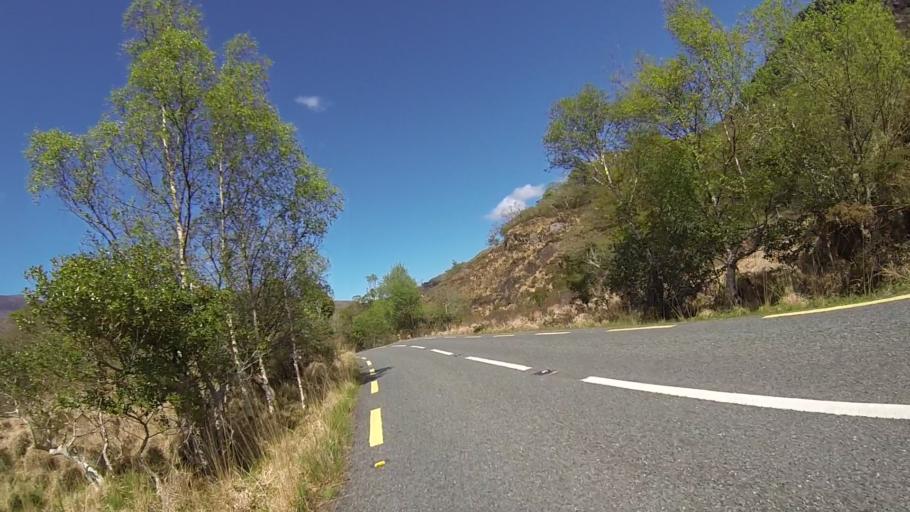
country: IE
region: Munster
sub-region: Ciarrai
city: Kenmare
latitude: 51.9759
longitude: -9.5768
